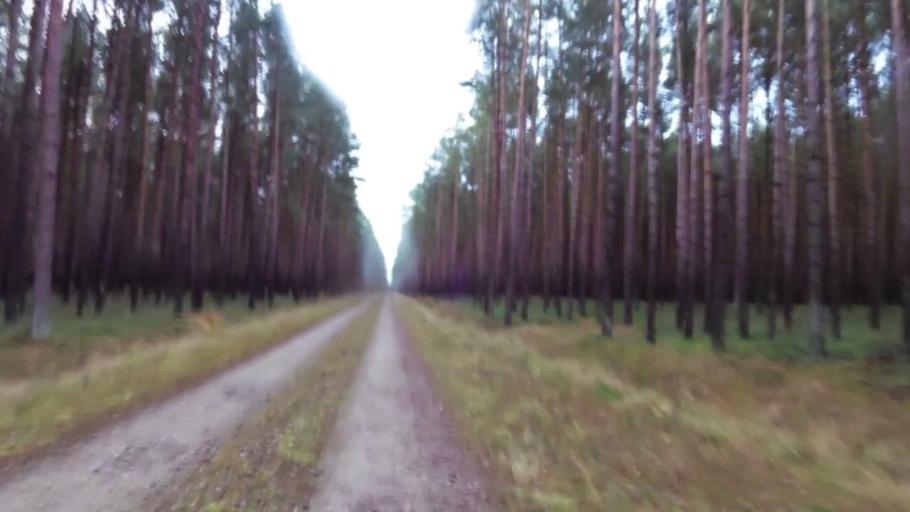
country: PL
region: West Pomeranian Voivodeship
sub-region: Powiat goleniowski
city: Stepnica
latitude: 53.6336
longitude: 14.7148
